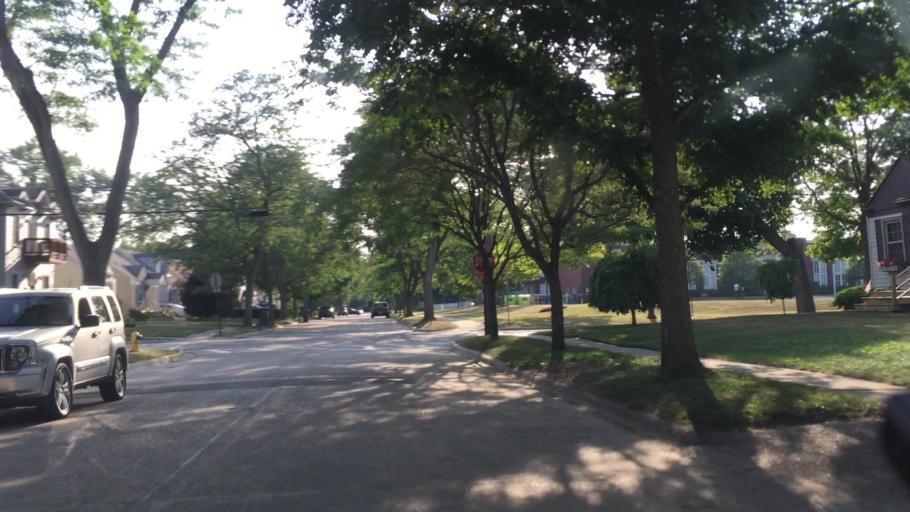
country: US
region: Michigan
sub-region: Oakland County
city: Birmingham
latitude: 42.5325
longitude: -83.2111
